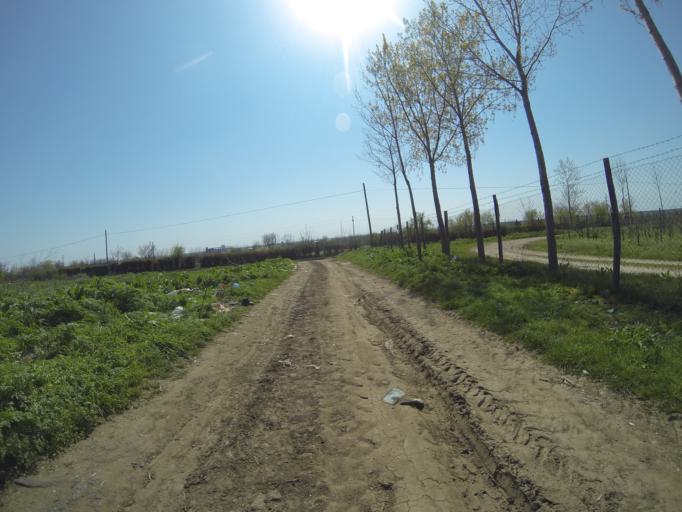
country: RO
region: Dolj
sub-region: Comuna Segarcea
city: Segarcea
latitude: 44.1007
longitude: 23.7254
